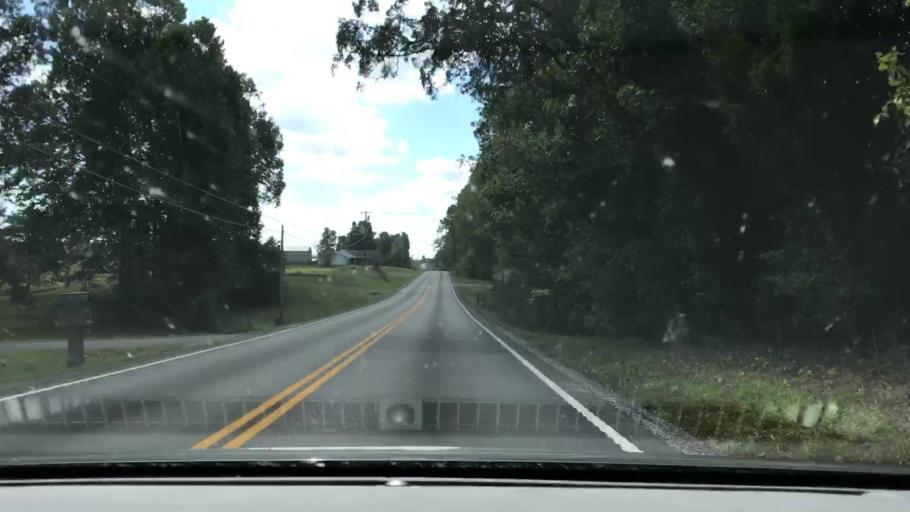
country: US
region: Kentucky
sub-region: Graves County
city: Mayfield
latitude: 36.7929
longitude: -88.5956
